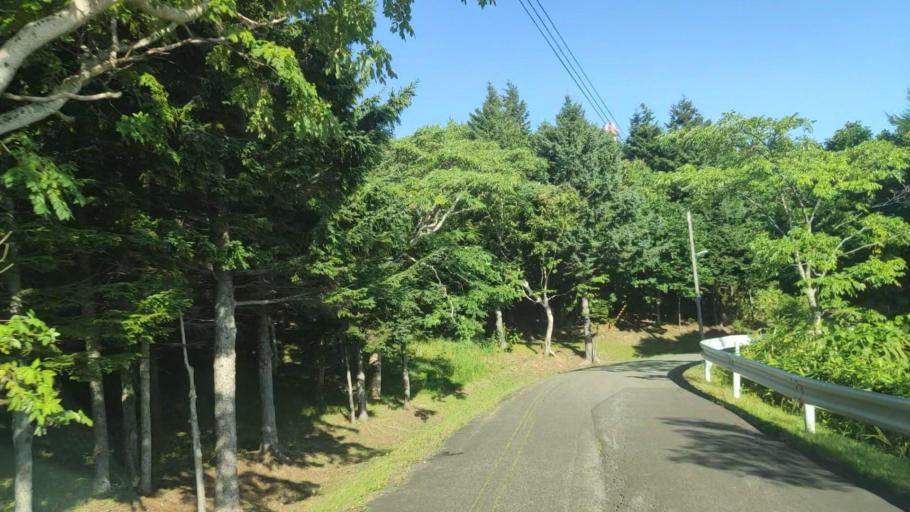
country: JP
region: Hokkaido
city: Wakkanai
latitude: 45.4132
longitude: 141.6689
